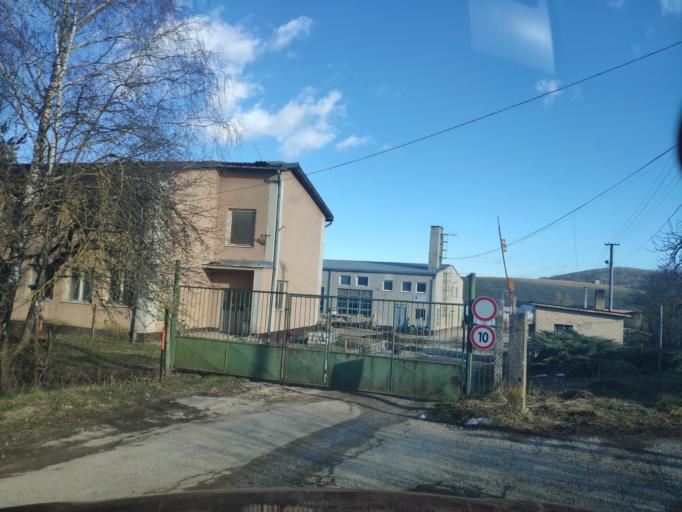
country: SK
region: Kosicky
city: Roznava
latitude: 48.5525
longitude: 20.5248
